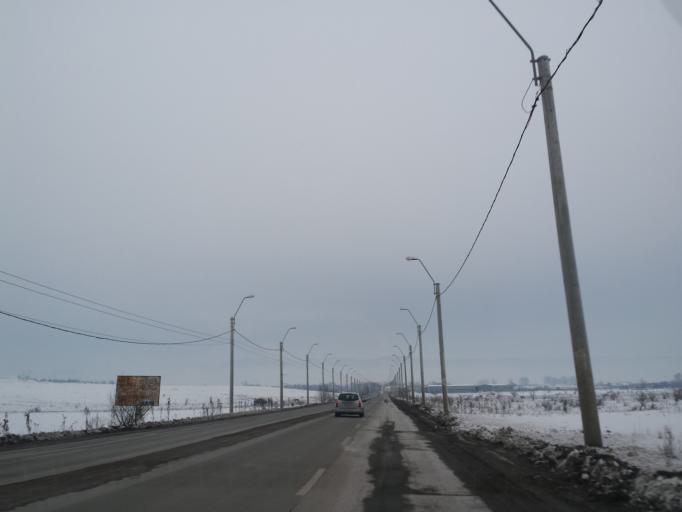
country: RO
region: Hunedoara
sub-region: Municipiul Deva
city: Cristur
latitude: 45.8459
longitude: 22.9504
